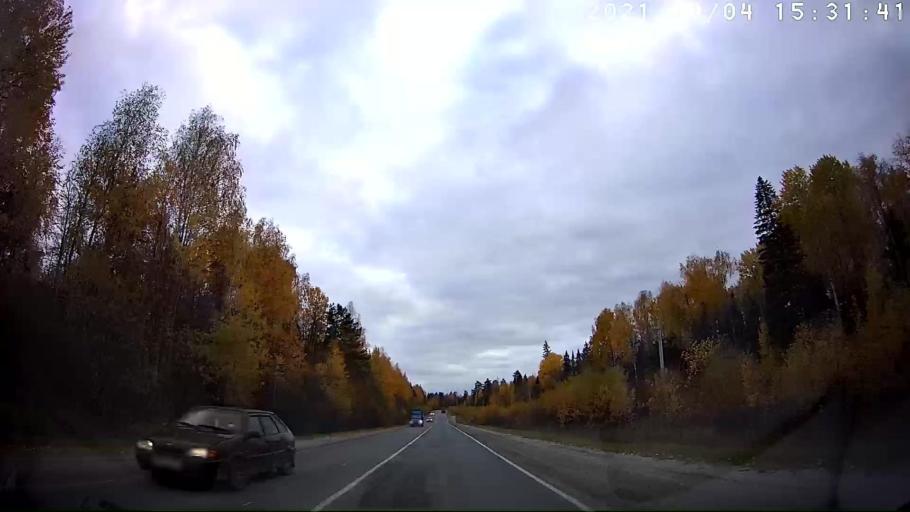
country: RU
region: Mariy-El
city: Yoshkar-Ola
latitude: 56.5766
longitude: 47.9716
